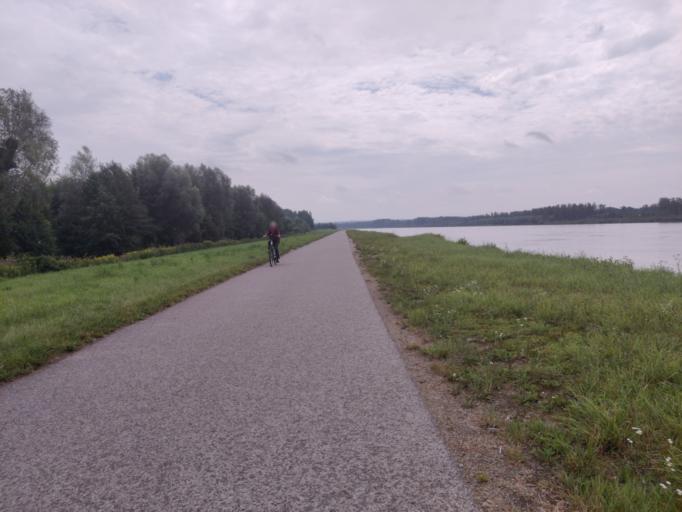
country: AT
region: Upper Austria
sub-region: Politischer Bezirk Perg
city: Perg
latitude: 48.2097
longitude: 14.6003
